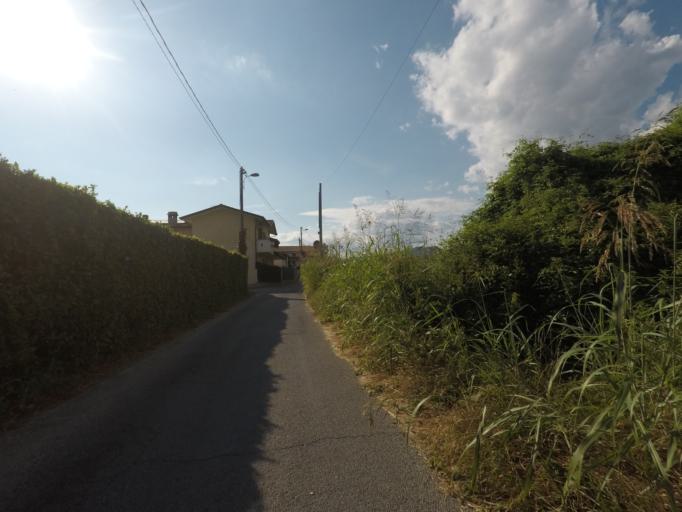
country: IT
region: Tuscany
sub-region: Provincia di Massa-Carrara
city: Capanne-Prato-Cinquale
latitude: 44.0135
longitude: 10.1444
